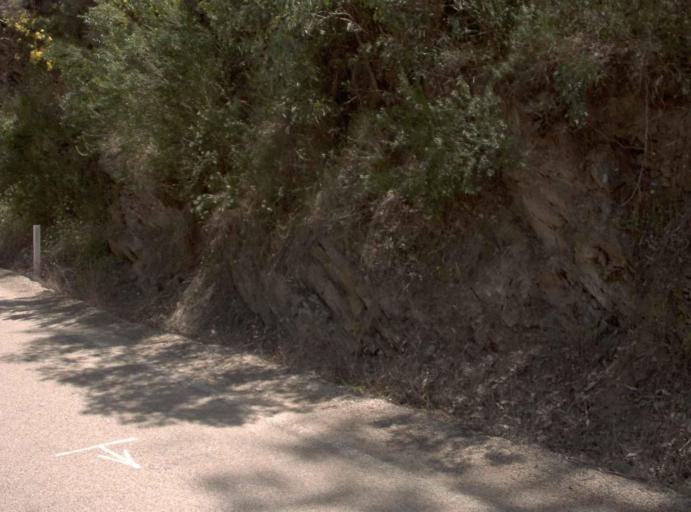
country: AU
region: Victoria
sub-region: East Gippsland
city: Bairnsdale
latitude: -37.4666
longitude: 147.8311
